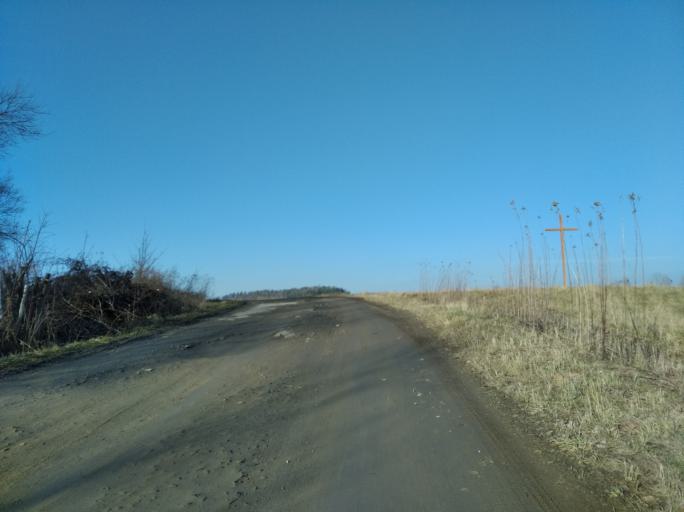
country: PL
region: Subcarpathian Voivodeship
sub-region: Powiat strzyzowski
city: Jawornik
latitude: 49.8294
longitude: 21.8702
